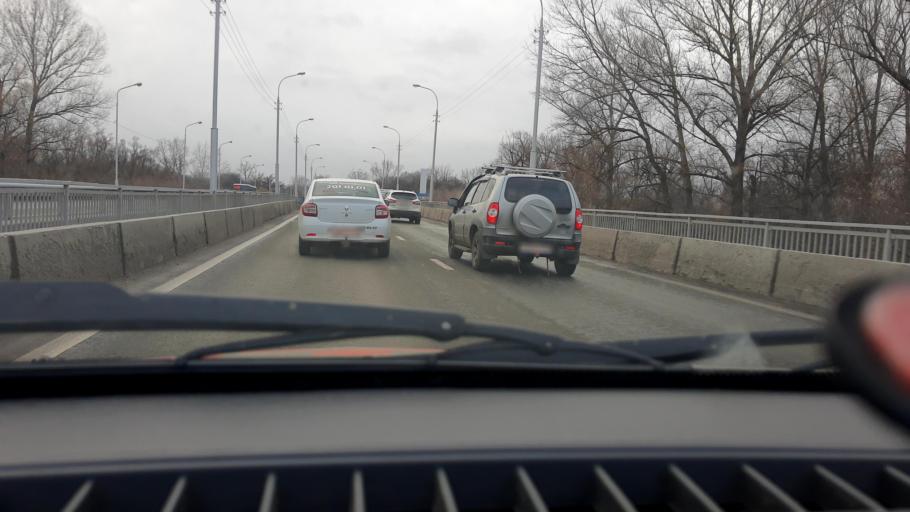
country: RU
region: Bashkortostan
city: Ufa
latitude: 54.6999
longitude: 55.9174
